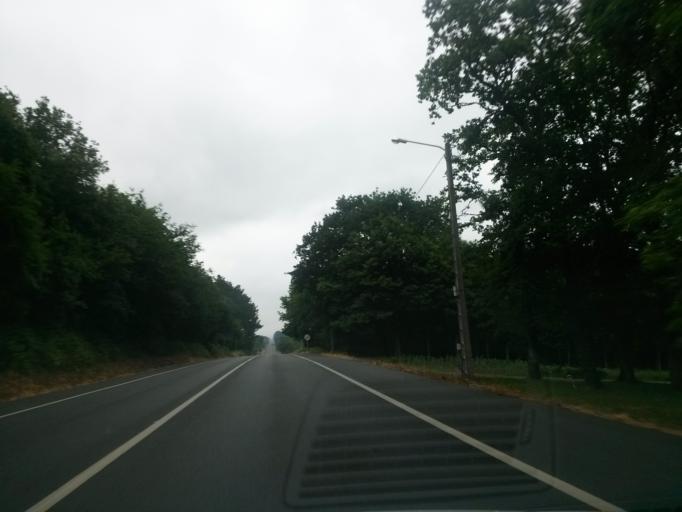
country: ES
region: Galicia
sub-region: Provincia de Lugo
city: Begonte
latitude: 43.1402
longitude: -7.6689
